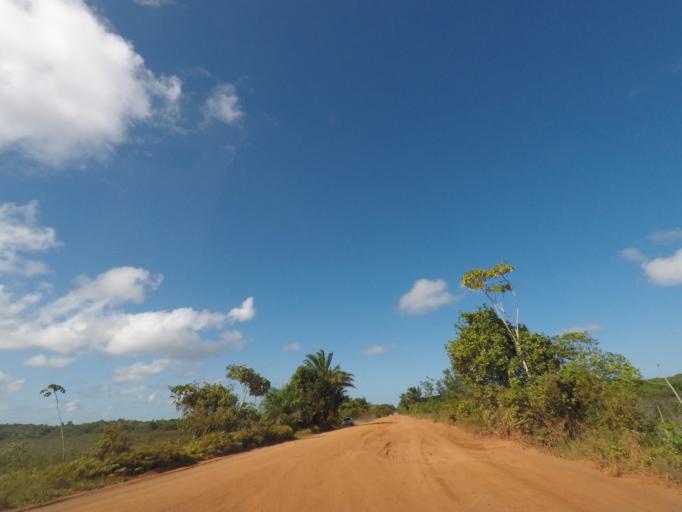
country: BR
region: Bahia
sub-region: Marau
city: Marau
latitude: -14.1436
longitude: -39.0022
